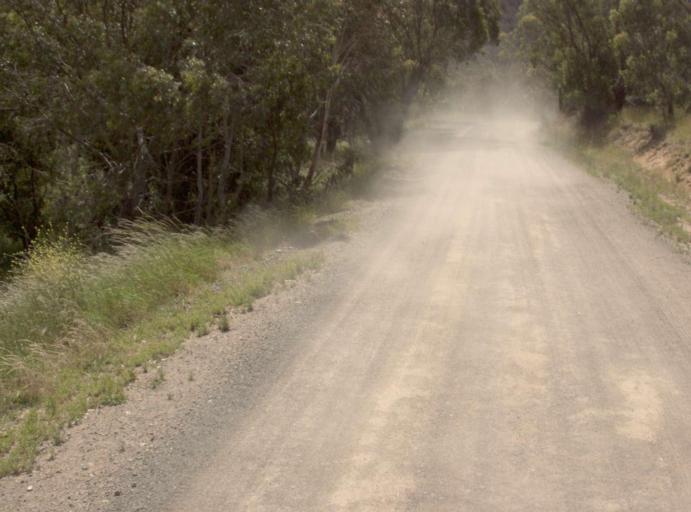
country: AU
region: New South Wales
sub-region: Bombala
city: Bombala
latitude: -37.1406
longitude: 148.6641
